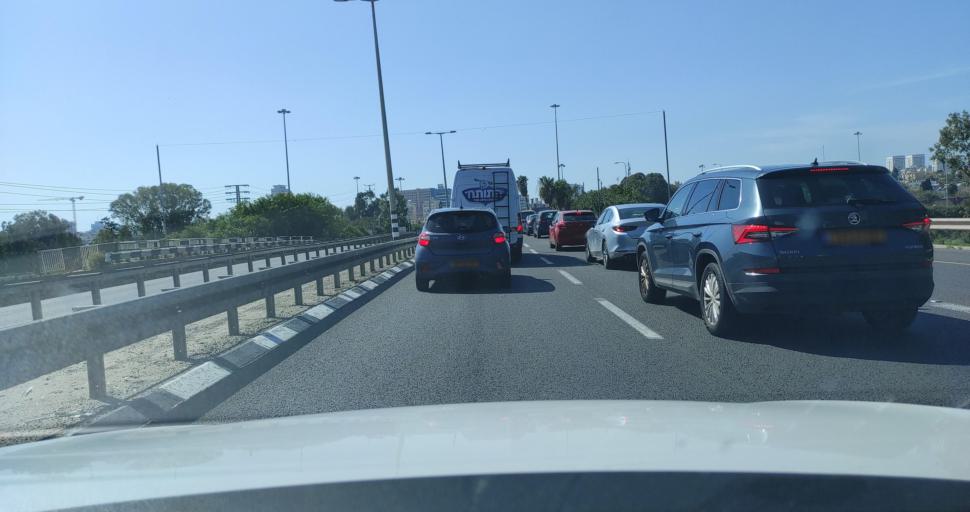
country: IL
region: Central District
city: Netanya
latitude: 32.3247
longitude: 34.8708
